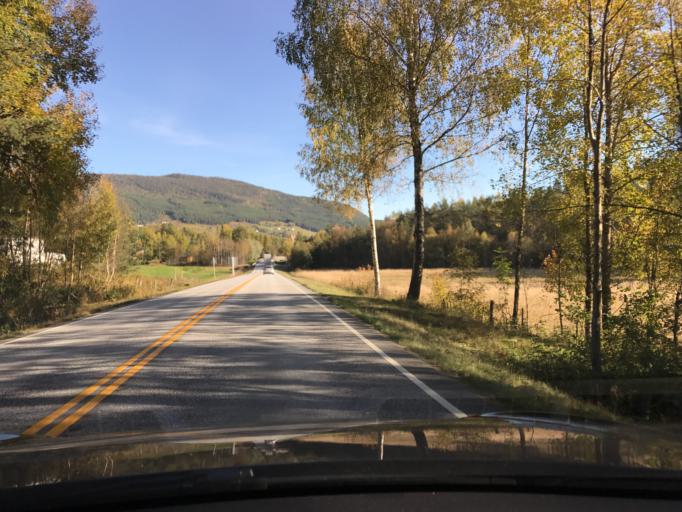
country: NO
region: Sogn og Fjordane
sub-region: Sogndal
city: Sogndalsfjora
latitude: 61.2064
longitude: 7.1948
